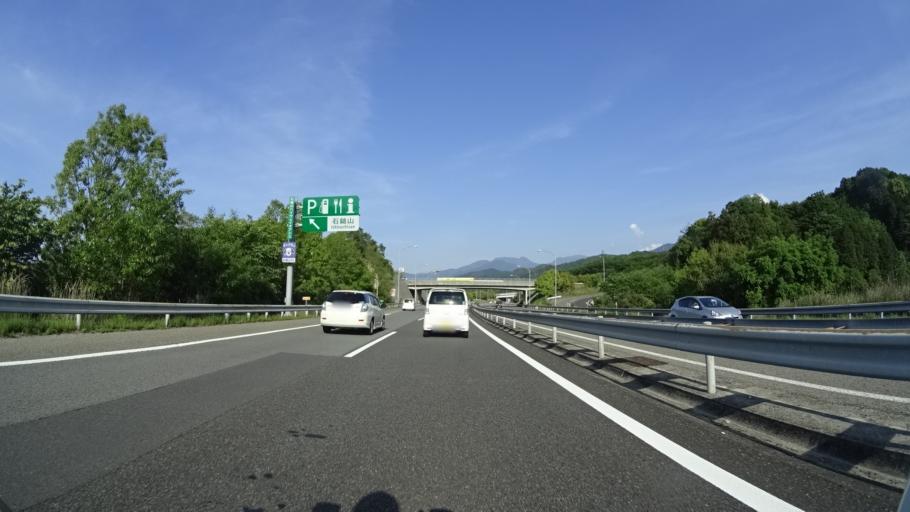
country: JP
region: Ehime
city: Saijo
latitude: 33.8858
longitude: 133.1054
